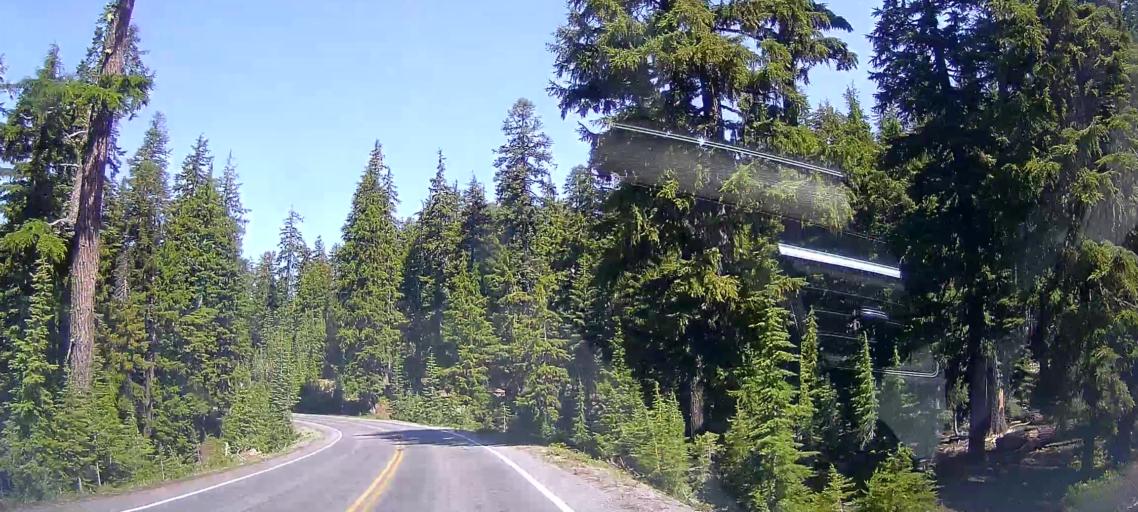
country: US
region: Oregon
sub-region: Jackson County
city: Shady Cove
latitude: 42.8805
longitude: -122.1240
